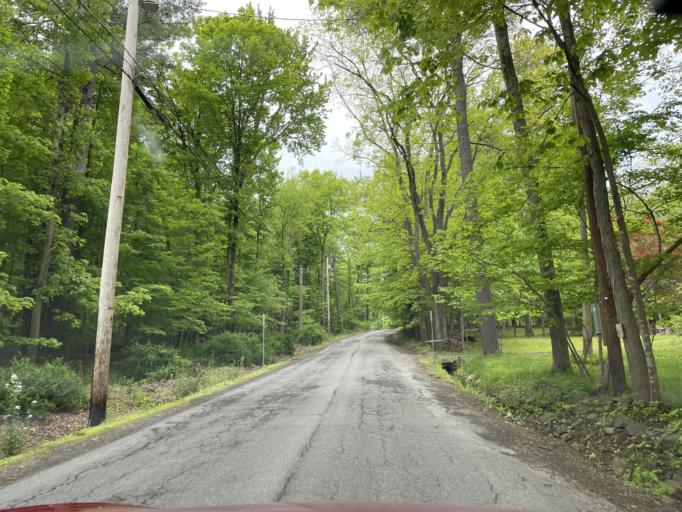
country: US
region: New York
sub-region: Ulster County
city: Woodstock
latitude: 42.0362
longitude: -74.1177
